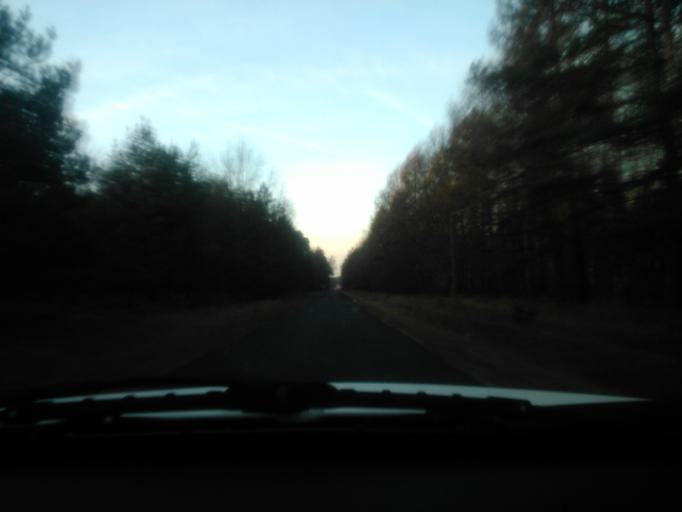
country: PL
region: Kujawsko-Pomorskie
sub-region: Powiat golubsko-dobrzynski
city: Golub-Dobrzyn
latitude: 53.1403
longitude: 19.1139
